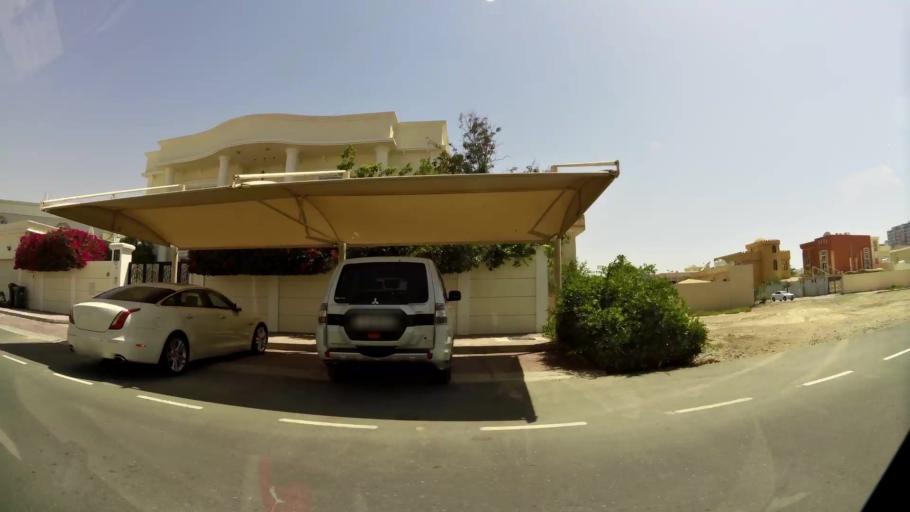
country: AE
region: Dubai
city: Dubai
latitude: 25.1096
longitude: 55.2102
